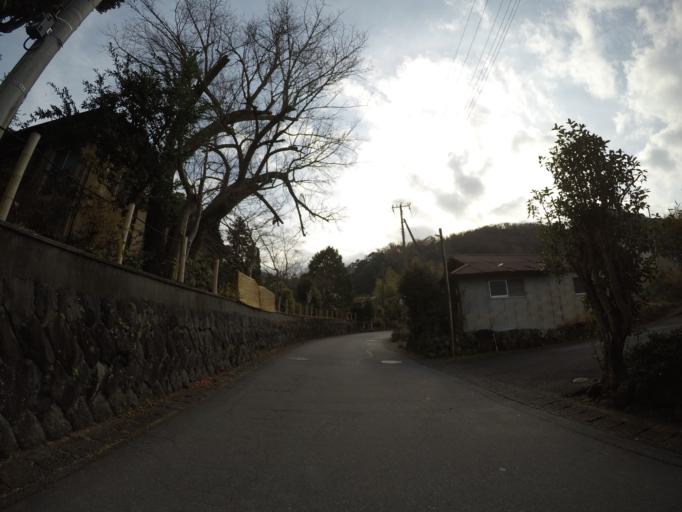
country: JP
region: Shizuoka
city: Heda
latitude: 34.8893
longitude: 138.9272
